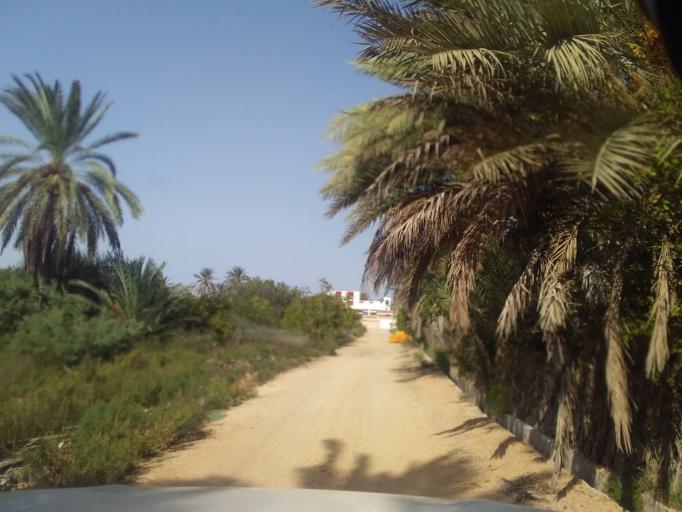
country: TN
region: Qabis
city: Gabes
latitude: 33.6293
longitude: 10.2867
